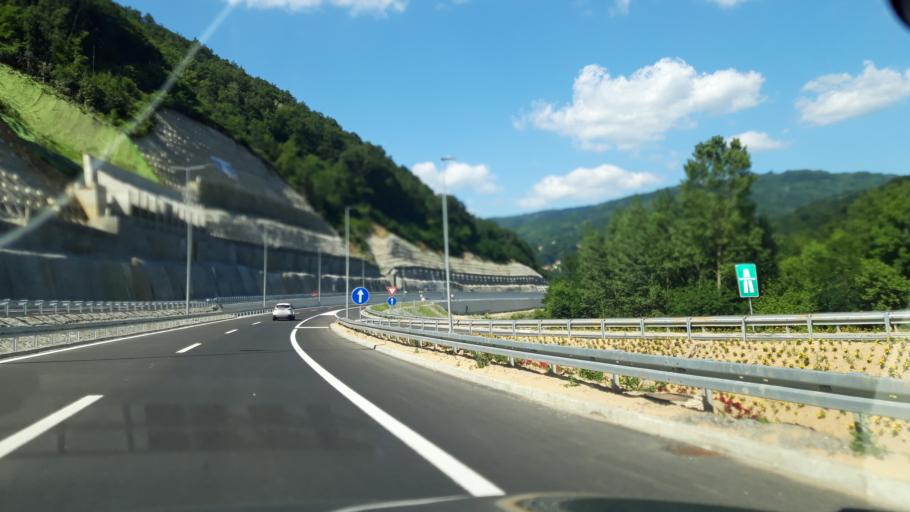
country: RS
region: Central Serbia
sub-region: Pcinjski Okrug
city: Vladicin Han
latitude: 42.8212
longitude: 22.1217
